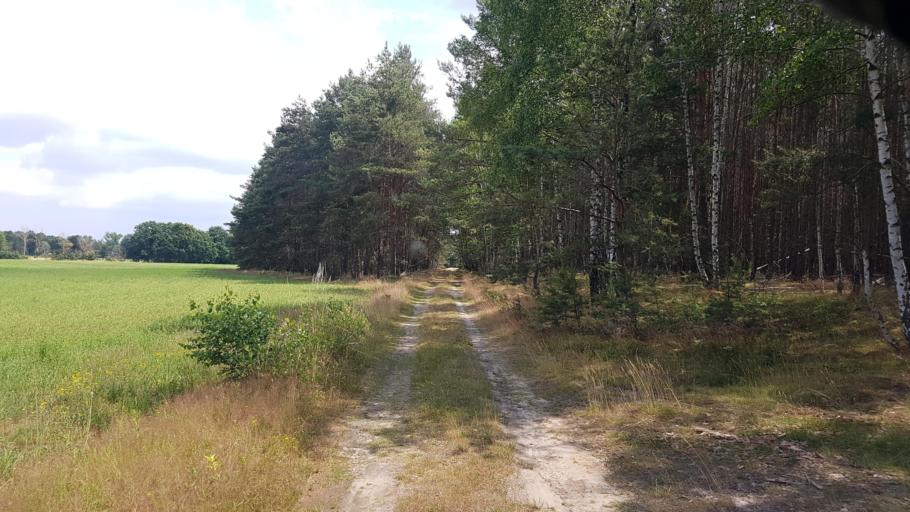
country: DE
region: Brandenburg
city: Crinitz
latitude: 51.7545
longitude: 13.8494
